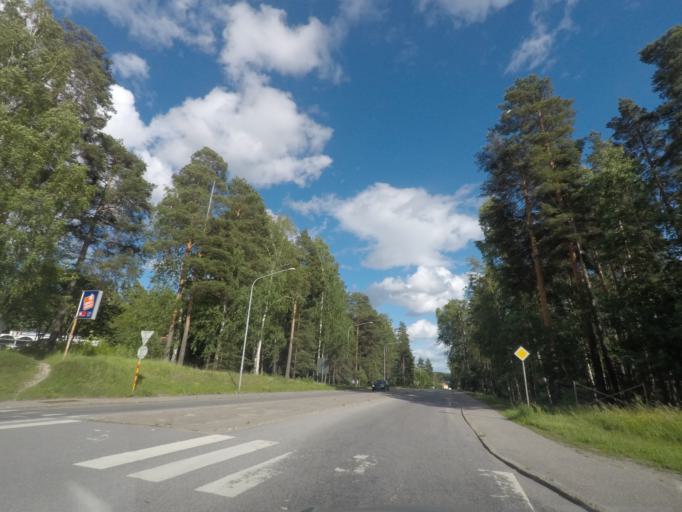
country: SE
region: OErebro
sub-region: Lindesbergs Kommun
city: Lindesberg
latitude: 59.6034
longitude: 15.2090
